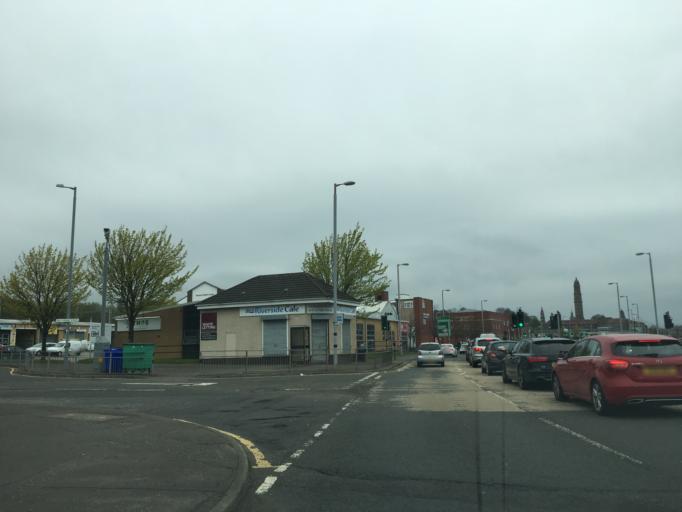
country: GB
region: Scotland
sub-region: Inverclyde
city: Greenock
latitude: 55.9438
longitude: -4.7449
